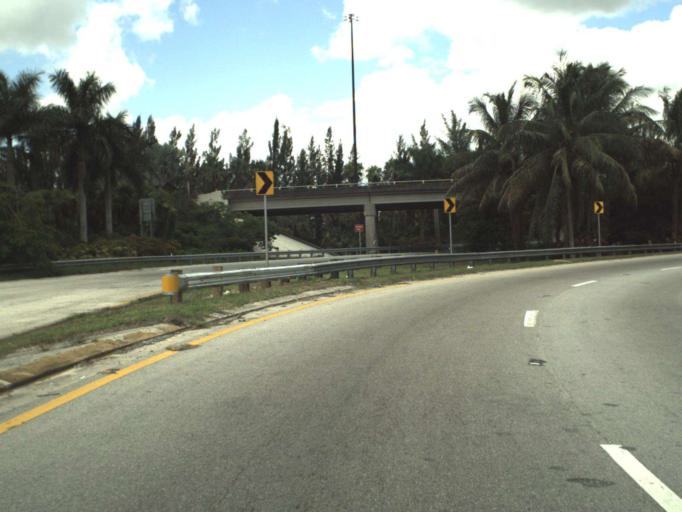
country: US
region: Florida
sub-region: Miami-Dade County
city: Golden Glades
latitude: 25.9219
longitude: -80.2133
